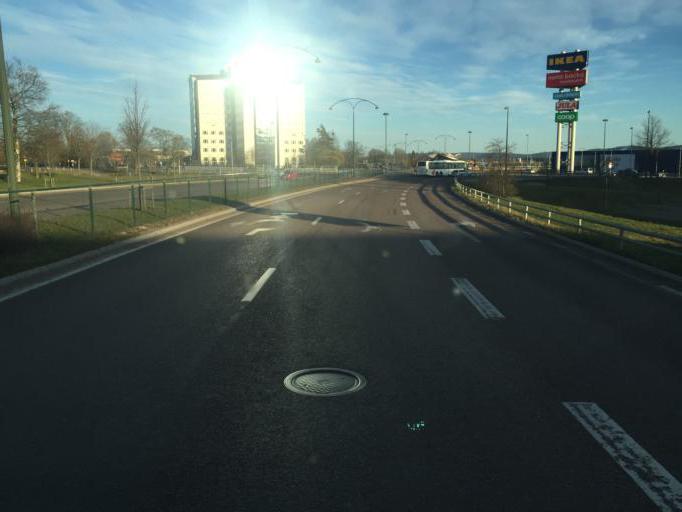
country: SE
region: Dalarna
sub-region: Borlange Kommun
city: Borlaenge
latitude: 60.4848
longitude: 15.4203
